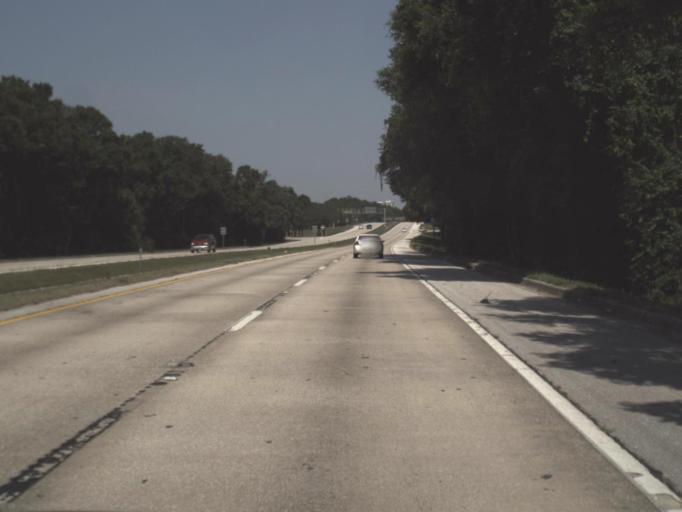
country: US
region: Florida
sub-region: Duval County
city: Jacksonville
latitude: 30.2946
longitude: -81.5962
